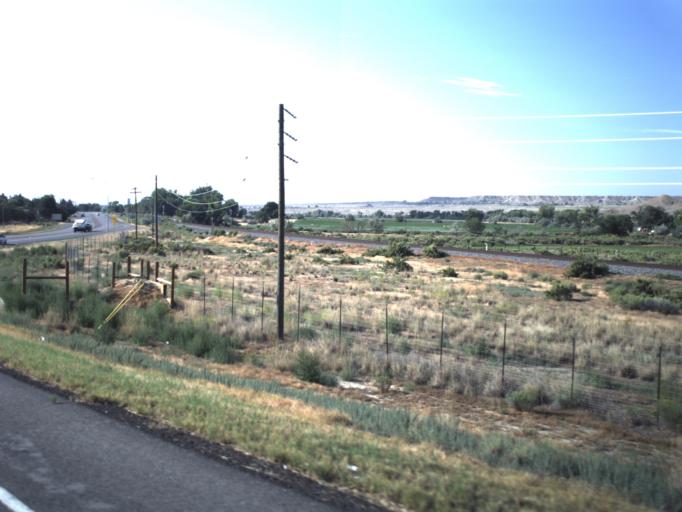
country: US
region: Utah
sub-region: Carbon County
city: Price
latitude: 39.5845
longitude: -110.7885
